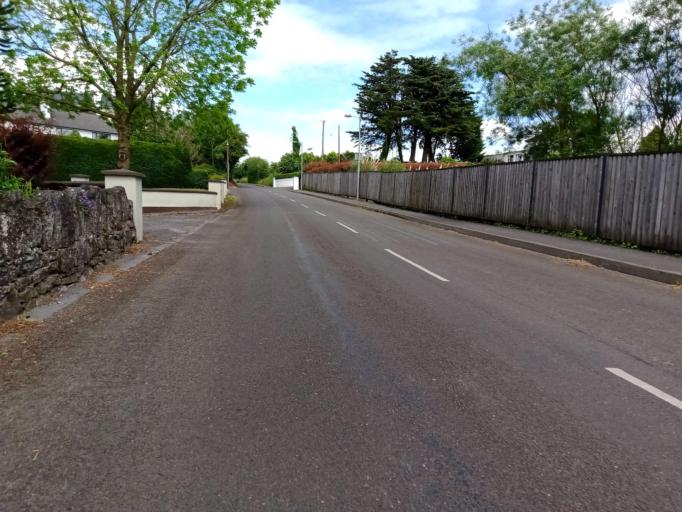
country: IE
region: Leinster
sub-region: Kilkenny
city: Kilkenny
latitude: 52.6747
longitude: -7.2492
